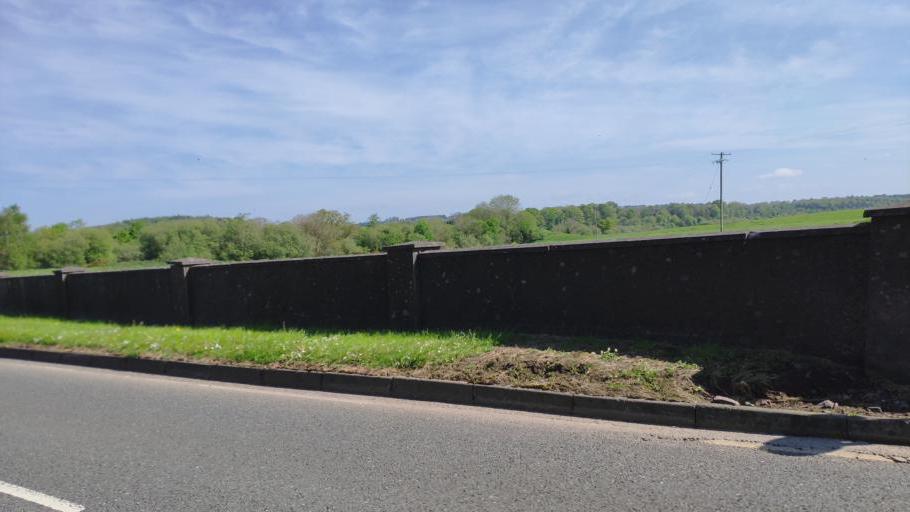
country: IE
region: Munster
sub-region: County Cork
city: Blarney
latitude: 51.9267
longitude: -8.5568
